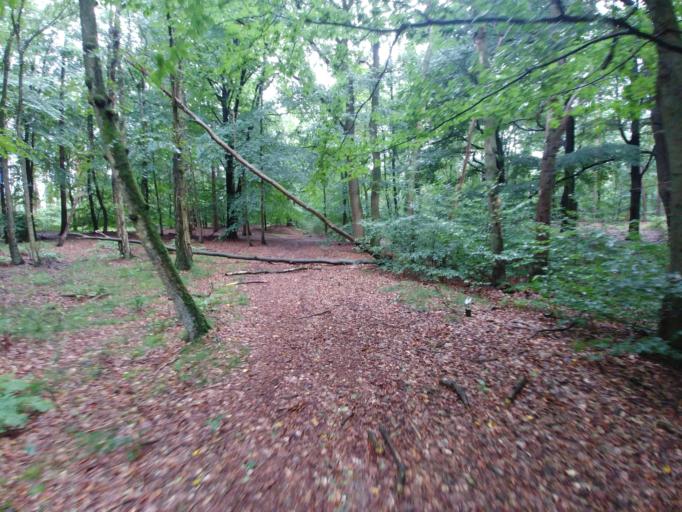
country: NL
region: Utrecht
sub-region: Gemeente Utrechtse Heuvelrug
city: Amerongen
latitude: 52.0176
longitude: 5.4620
